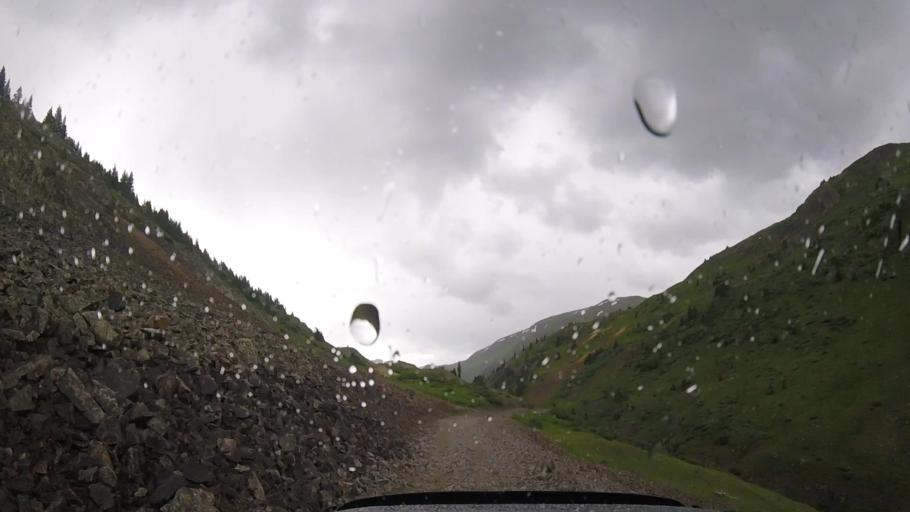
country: US
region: Colorado
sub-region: Ouray County
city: Ouray
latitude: 37.9415
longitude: -107.5735
